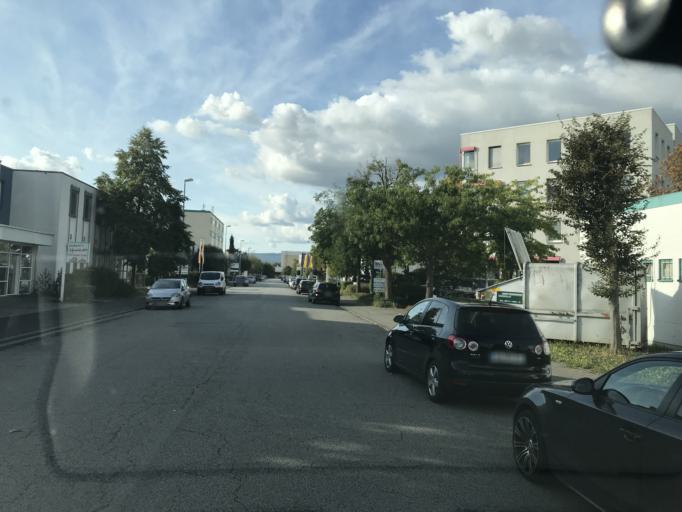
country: DE
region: Rheinland-Pfalz
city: Mainz
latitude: 50.0260
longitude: 8.2762
